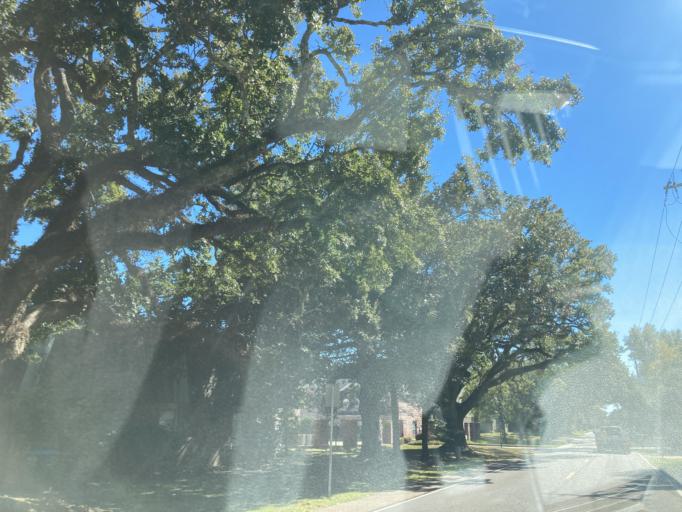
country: US
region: Mississippi
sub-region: Jackson County
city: Ocean Springs
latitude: 30.4095
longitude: -88.8102
